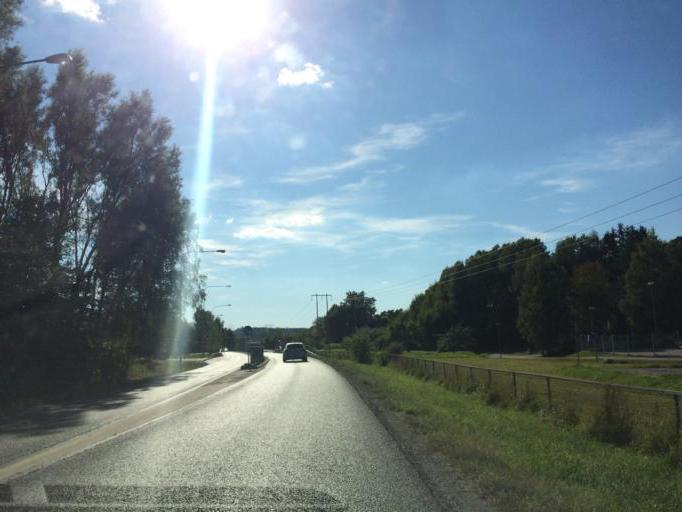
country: SE
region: Stockholm
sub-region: Upplands Vasby Kommun
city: Upplands Vaesby
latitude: 59.5005
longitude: 17.9403
